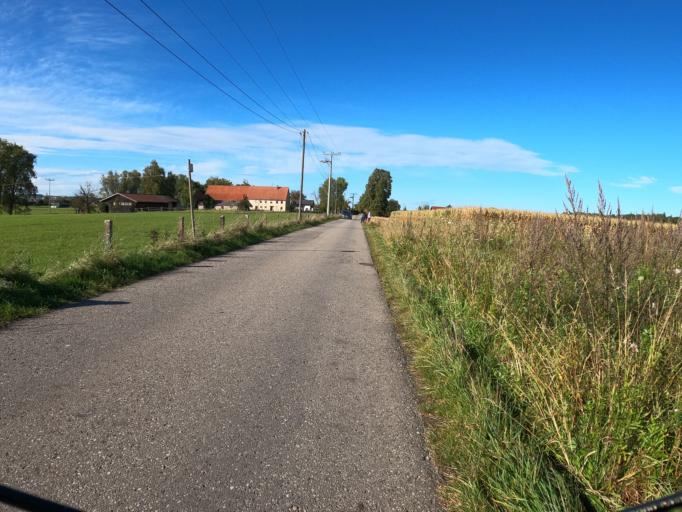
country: DE
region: Bavaria
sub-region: Swabia
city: Nersingen
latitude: 48.4174
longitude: 10.1410
